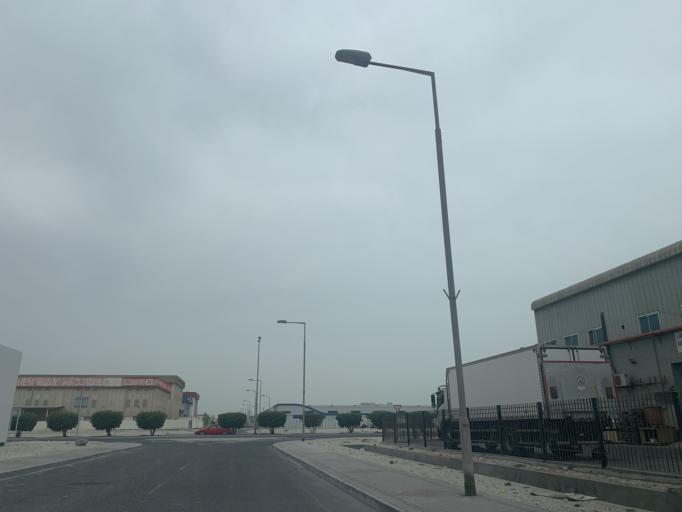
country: BH
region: Muharraq
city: Al Hadd
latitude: 26.2119
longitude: 50.6801
